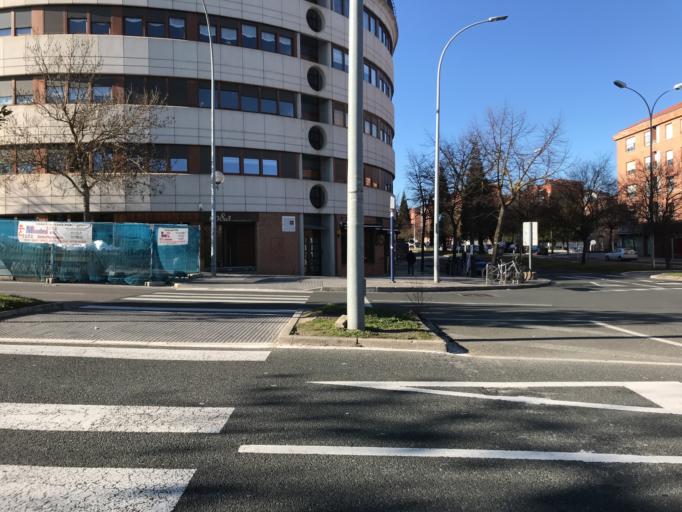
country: ES
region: Basque Country
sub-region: Provincia de Alava
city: Gasteiz / Vitoria
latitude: 42.8397
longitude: -2.6908
